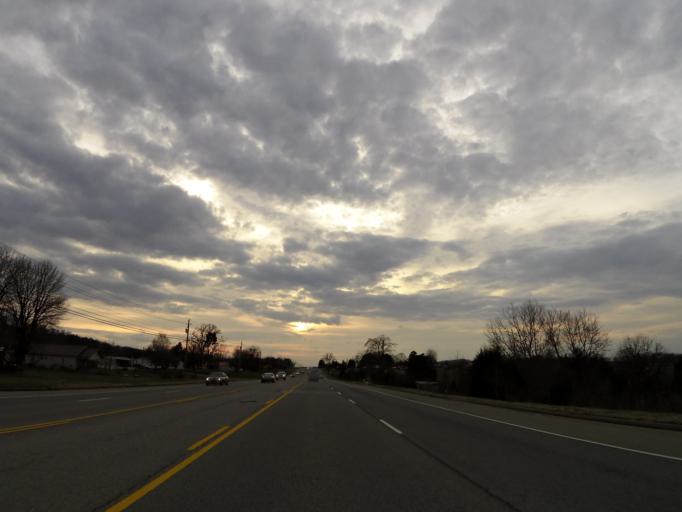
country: US
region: Tennessee
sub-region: Loudon County
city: Greenback
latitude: 35.6309
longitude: -84.1715
